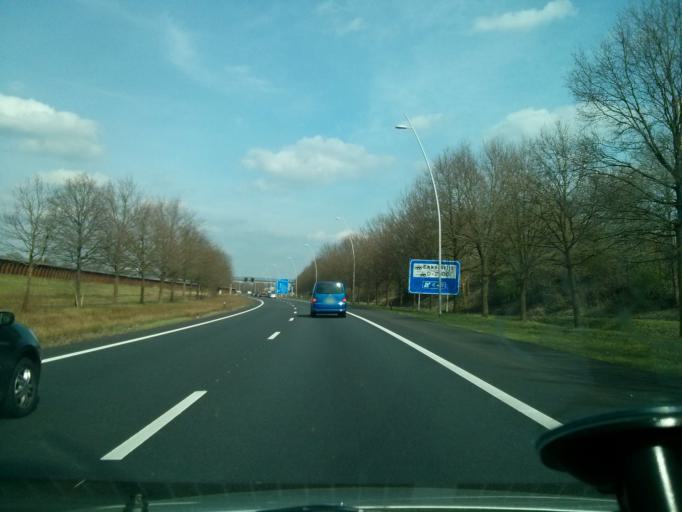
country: NL
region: North Brabant
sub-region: Gemeente Best
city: Best
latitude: 51.4923
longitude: 5.4383
